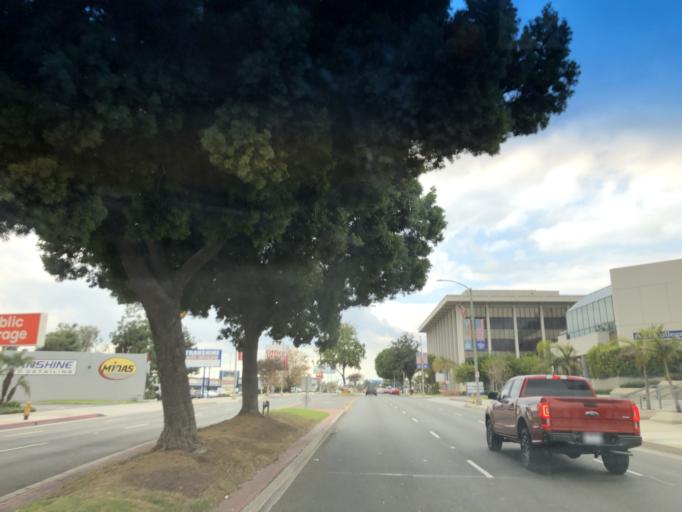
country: US
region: California
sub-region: Los Angeles County
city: East La Mirada
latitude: 33.9480
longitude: -118.0035
